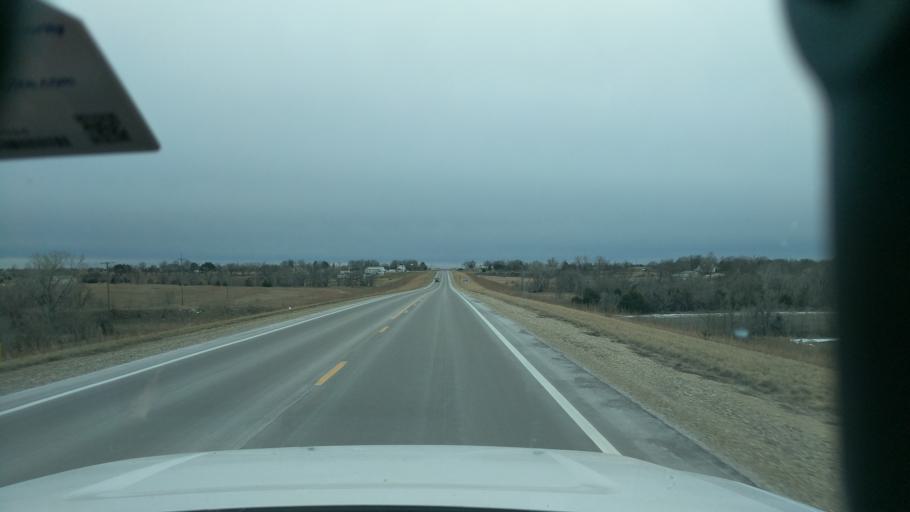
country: US
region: Kansas
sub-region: Dickinson County
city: Herington
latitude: 38.6740
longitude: -96.9309
